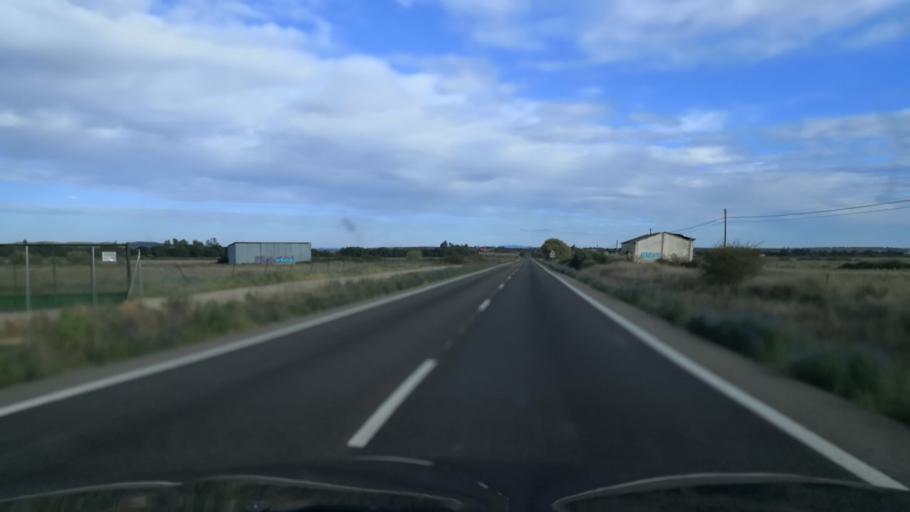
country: ES
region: Extremadura
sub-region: Provincia de Caceres
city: Huelaga
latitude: 40.0503
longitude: -6.6394
